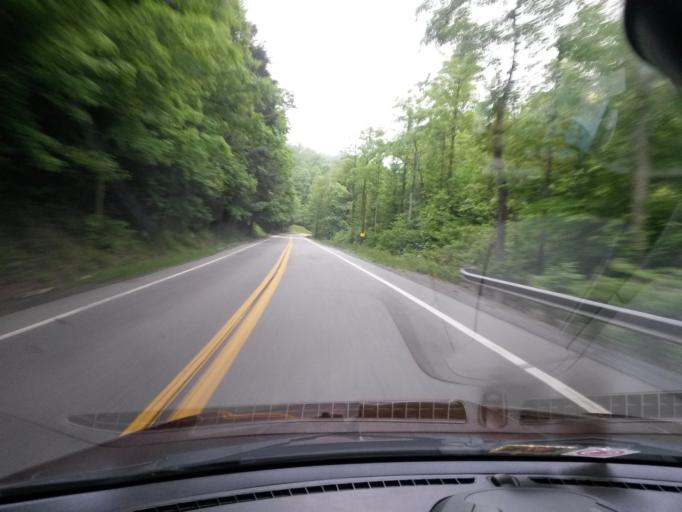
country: US
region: West Virginia
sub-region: Wyoming County
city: Pineville
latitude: 37.5525
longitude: -81.5693
